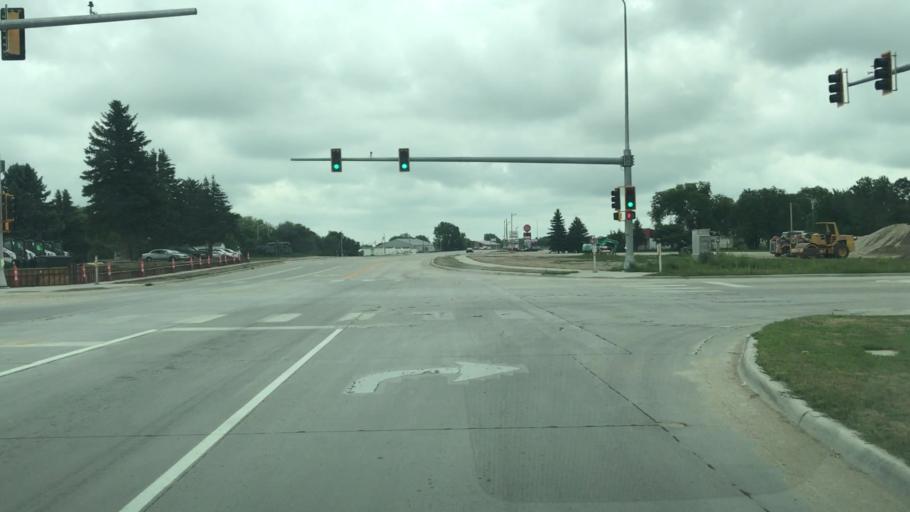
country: US
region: South Dakota
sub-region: Todd County
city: Mission
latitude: 43.3058
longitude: -100.6530
